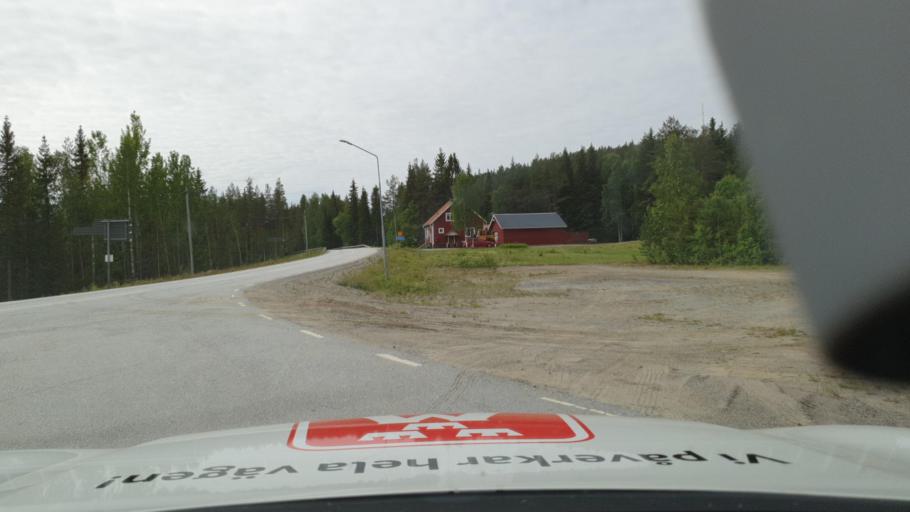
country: SE
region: Vaesterbotten
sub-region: Umea Kommun
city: Ersmark
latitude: 64.3277
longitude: 20.2241
